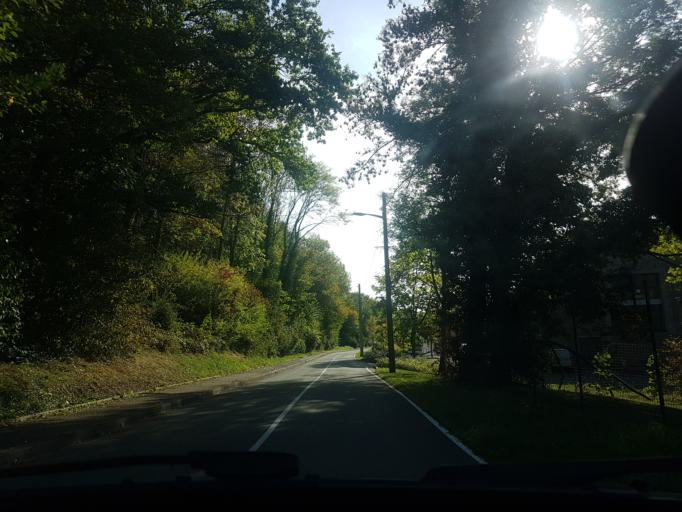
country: FR
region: Franche-Comte
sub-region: Territoire de Belfort
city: Belfort
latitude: 47.6468
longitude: 6.8656
